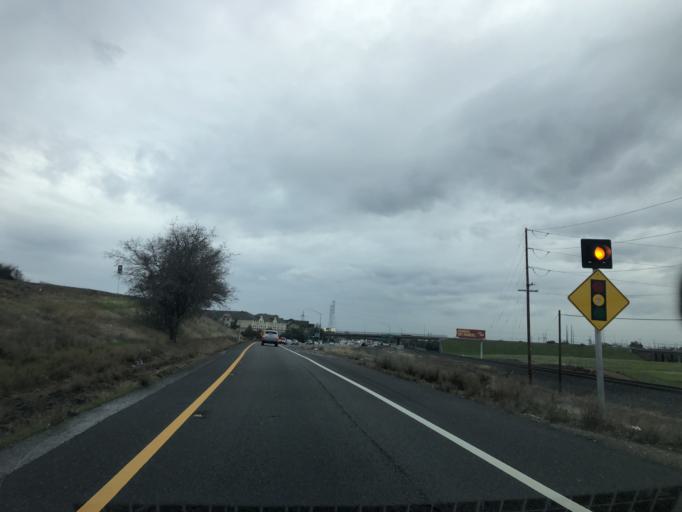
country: US
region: California
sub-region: Placer County
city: Rocklin
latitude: 38.7671
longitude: -121.2558
